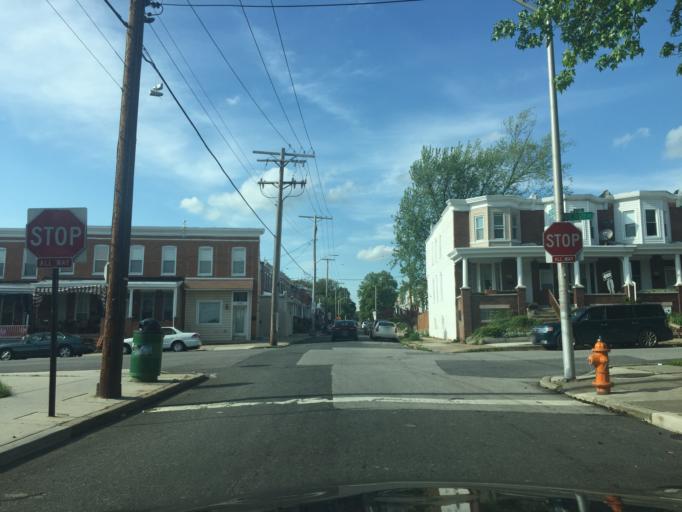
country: US
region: Maryland
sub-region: City of Baltimore
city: Baltimore
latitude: 39.3307
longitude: -76.6081
